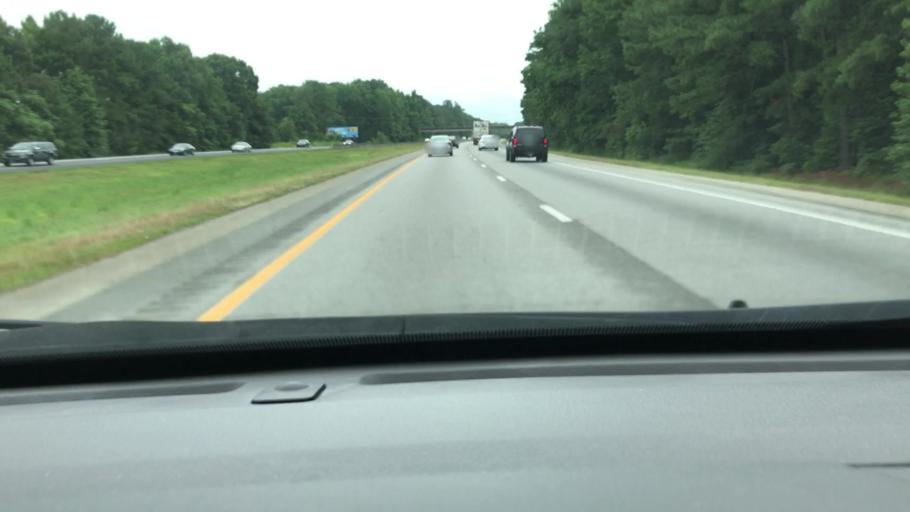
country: US
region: North Carolina
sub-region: Northampton County
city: Gaston
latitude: 36.5024
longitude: -77.5963
